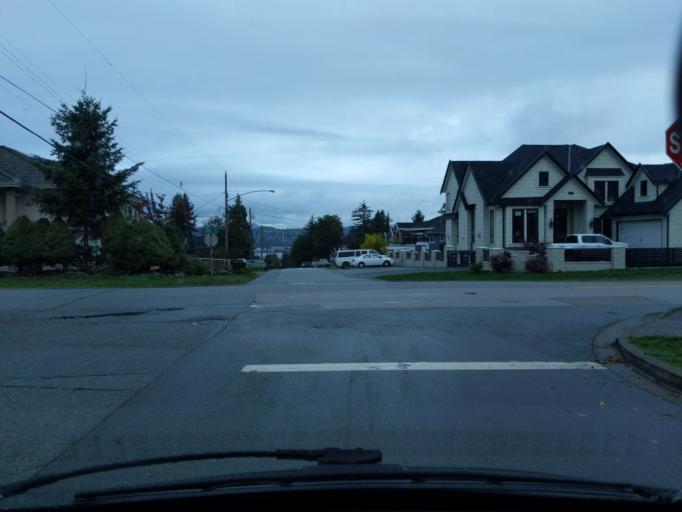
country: CA
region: British Columbia
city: New Westminster
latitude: 49.2008
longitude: -122.8620
